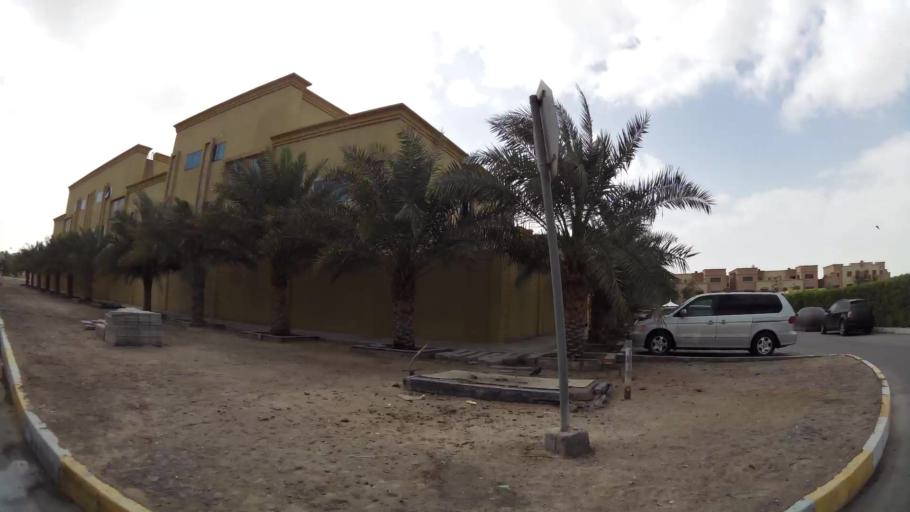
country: AE
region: Abu Dhabi
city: Abu Dhabi
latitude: 24.4141
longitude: 54.4953
